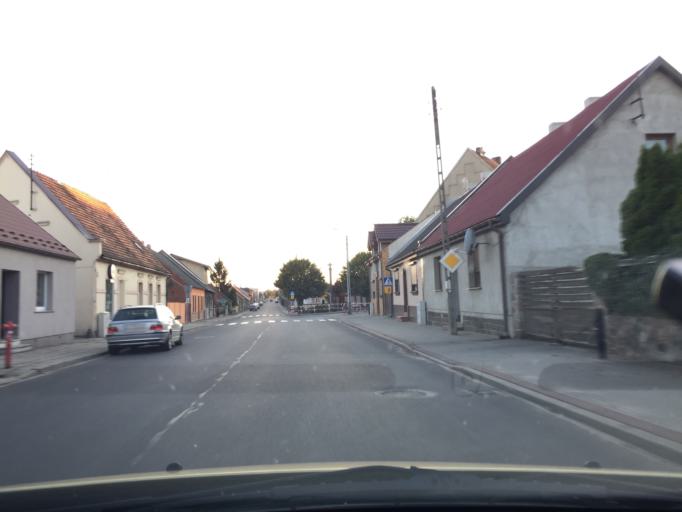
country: PL
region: Greater Poland Voivodeship
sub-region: Powiat pleszewski
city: Dobrzyca
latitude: 51.8660
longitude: 17.5986
